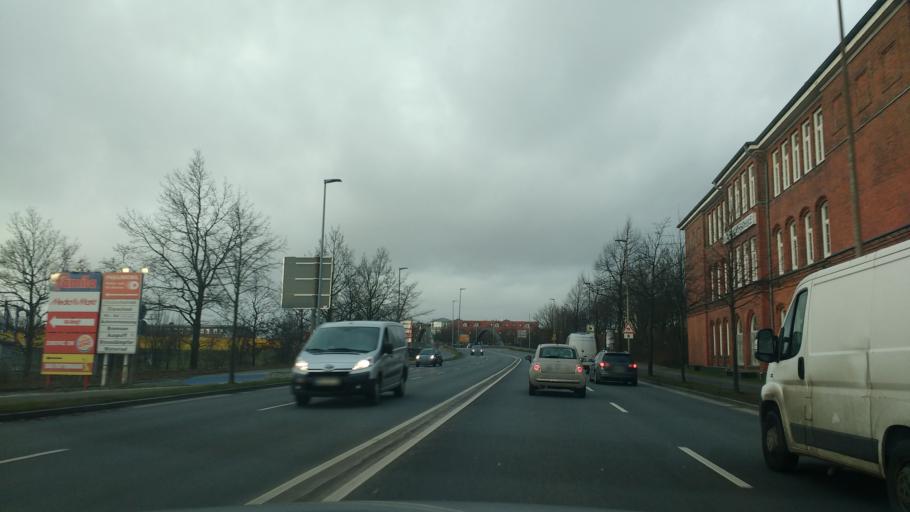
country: DE
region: Schleswig-Holstein
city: Itzehoe
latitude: 53.9155
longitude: 9.5159
